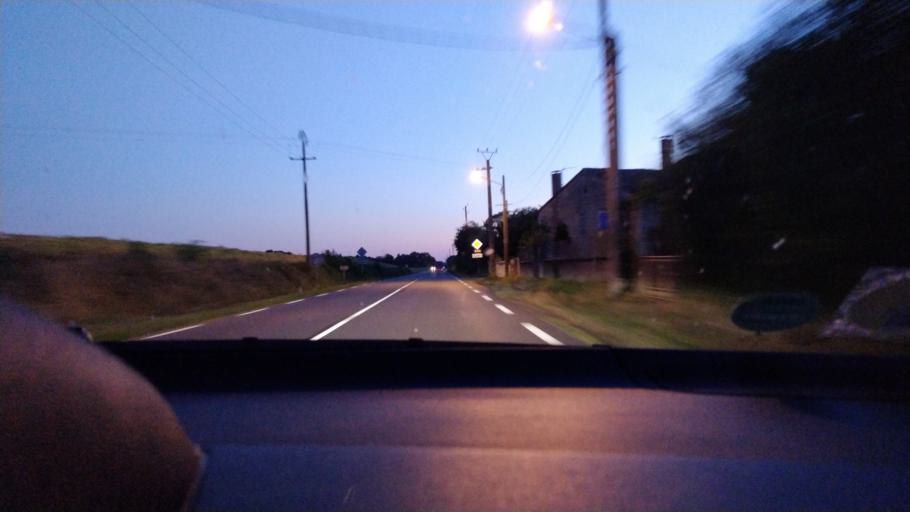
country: FR
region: Poitou-Charentes
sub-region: Departement de la Charente
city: Saint-Claud
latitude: 45.8483
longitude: 0.5001
